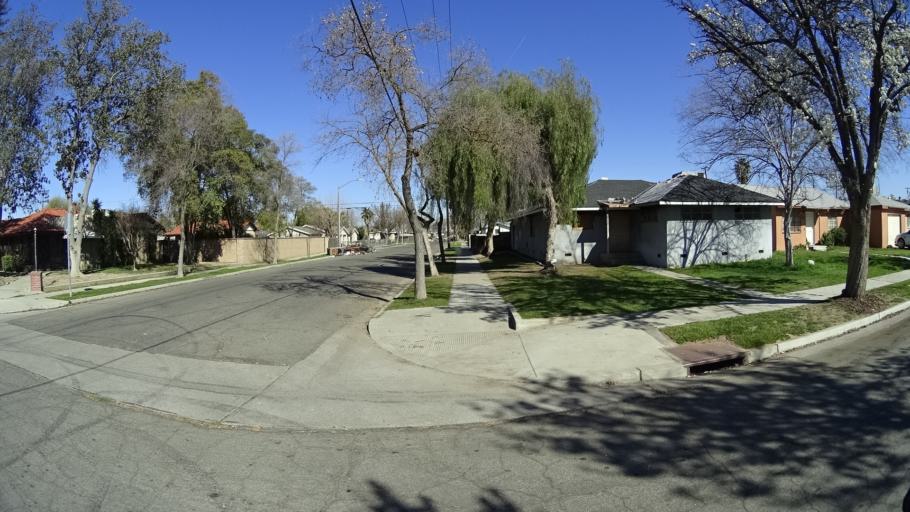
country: US
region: California
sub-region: Fresno County
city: West Park
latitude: 36.7236
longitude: -119.8153
